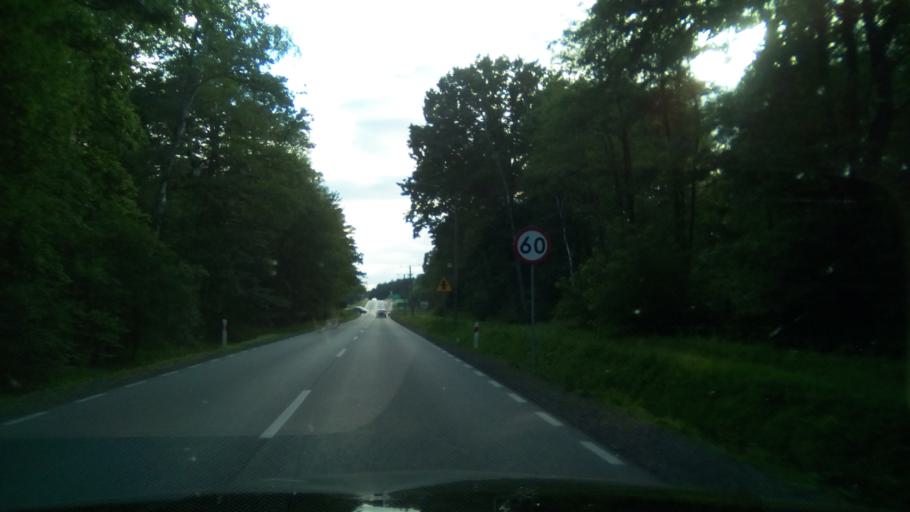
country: PL
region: Masovian Voivodeship
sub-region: Powiat bialobrzeski
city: Bialobrzegi
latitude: 51.6501
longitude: 20.9777
